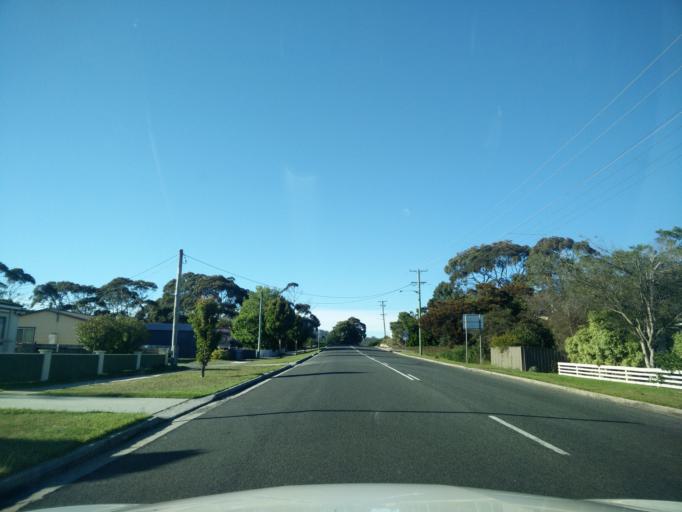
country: AU
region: Tasmania
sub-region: Break O'Day
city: St Helens
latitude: -41.8779
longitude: 148.3036
